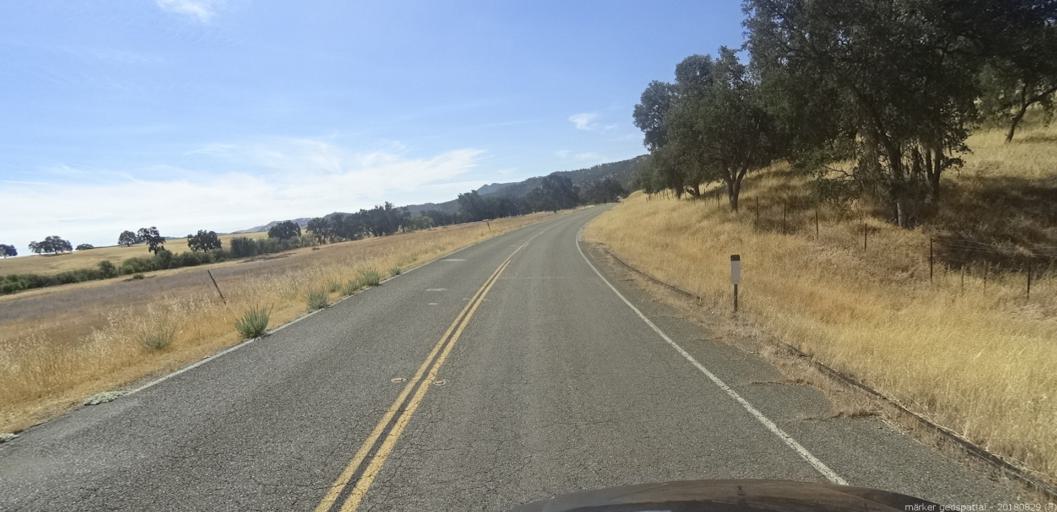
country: US
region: California
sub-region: San Luis Obispo County
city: Lake Nacimiento
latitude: 35.8202
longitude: -121.0091
